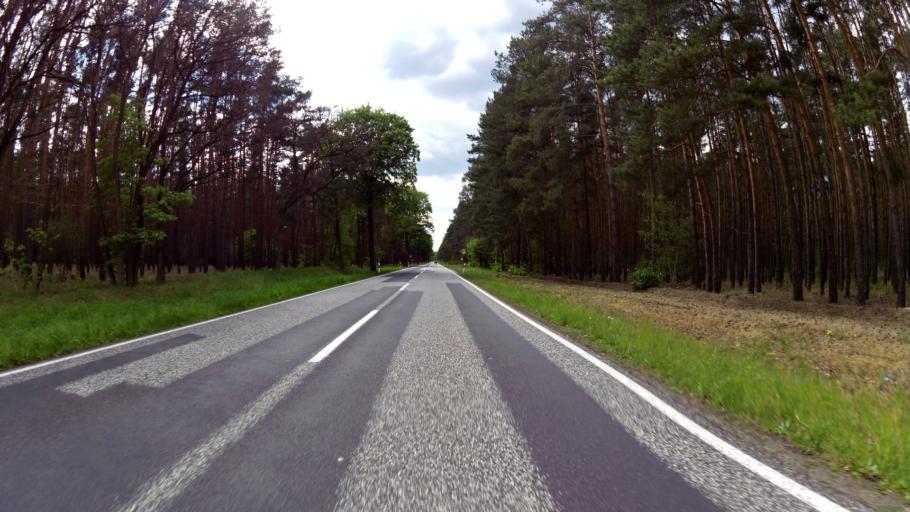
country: DE
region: Brandenburg
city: Spreenhagen
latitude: 52.3231
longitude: 13.9186
